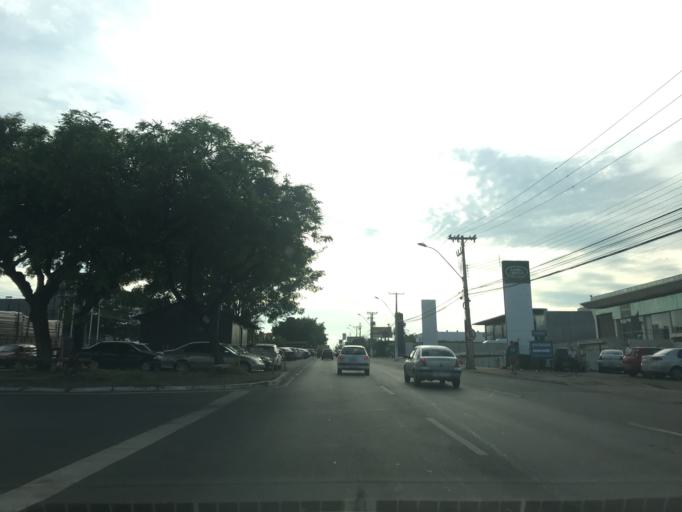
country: BR
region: Federal District
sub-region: Brasilia
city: Brasilia
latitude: -15.8050
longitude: -47.9670
